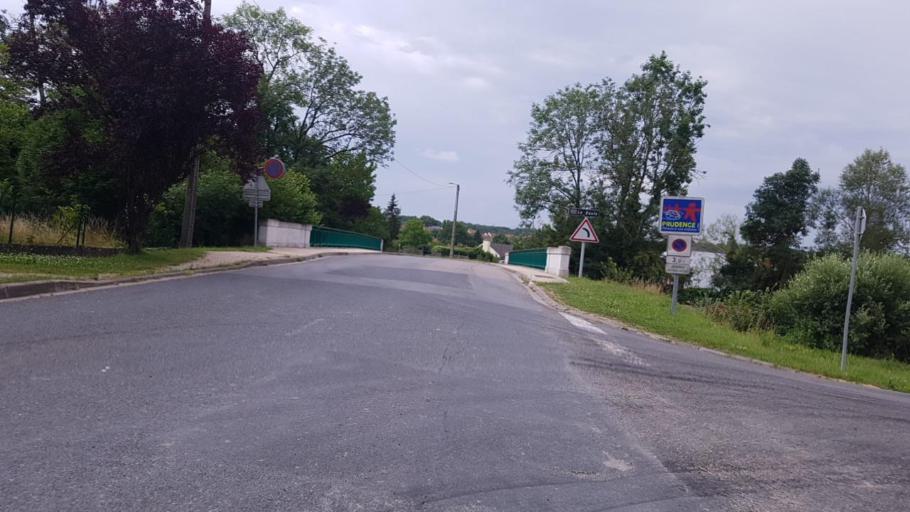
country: FR
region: Champagne-Ardenne
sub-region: Departement de la Marne
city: Sermaize-les-Bains
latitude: 48.7881
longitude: 4.9056
